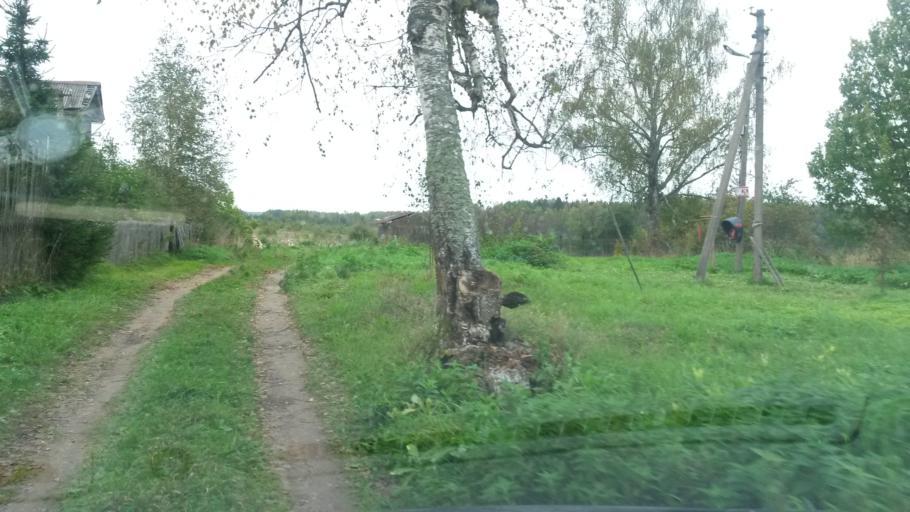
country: RU
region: Jaroslavl
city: Tutayev
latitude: 57.9501
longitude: 39.4262
